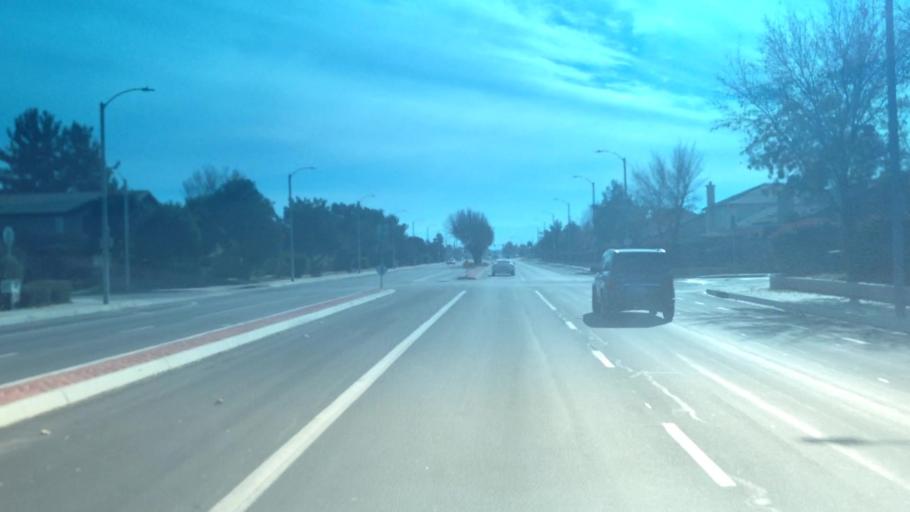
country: US
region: California
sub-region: Los Angeles County
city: Lancaster
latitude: 34.7085
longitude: -118.1661
